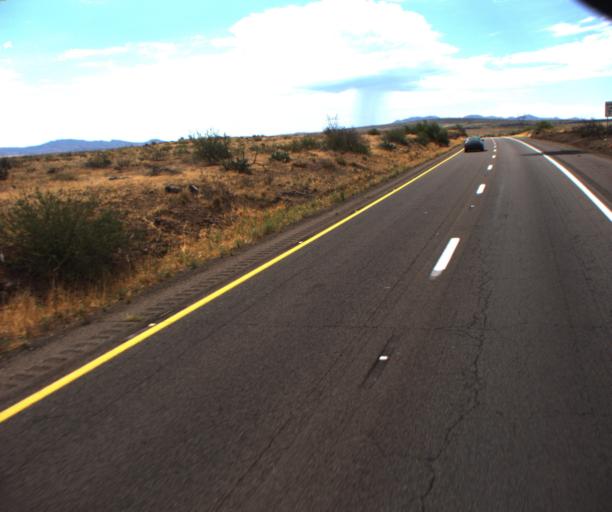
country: US
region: Arizona
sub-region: Yavapai County
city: Cordes Lakes
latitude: 34.2257
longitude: -112.1146
